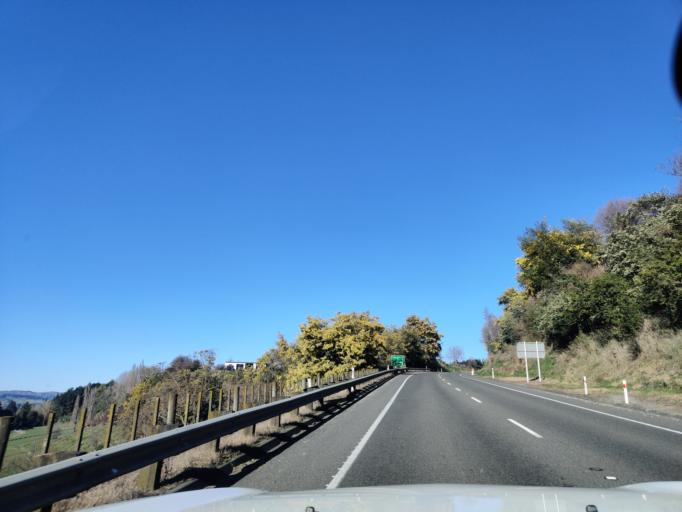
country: NZ
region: Manawatu-Wanganui
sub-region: Rangitikei District
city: Bulls
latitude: -39.9217
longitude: 175.6319
